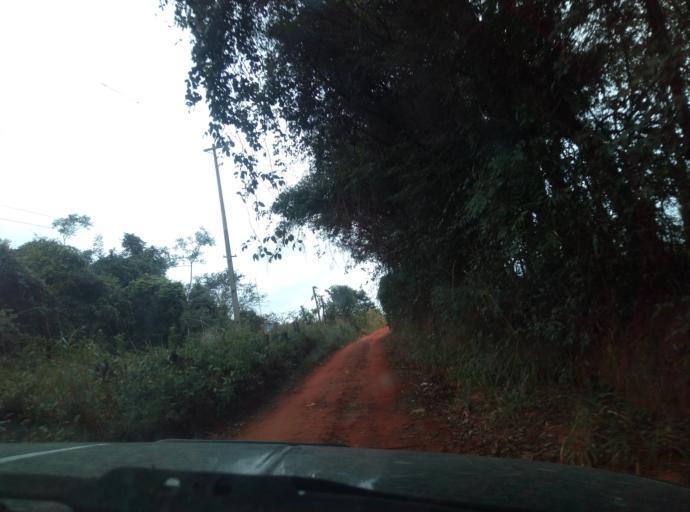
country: PY
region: Caaguazu
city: Doctor Cecilio Baez
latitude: -25.1578
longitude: -56.2716
